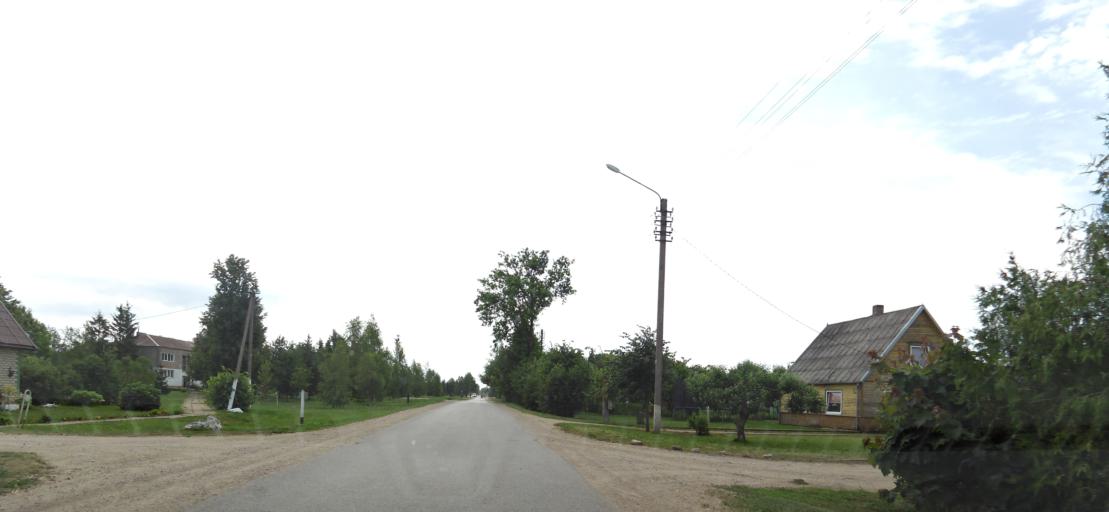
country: LT
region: Panevezys
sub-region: Birzai
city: Birzai
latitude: 56.2650
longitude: 24.6079
